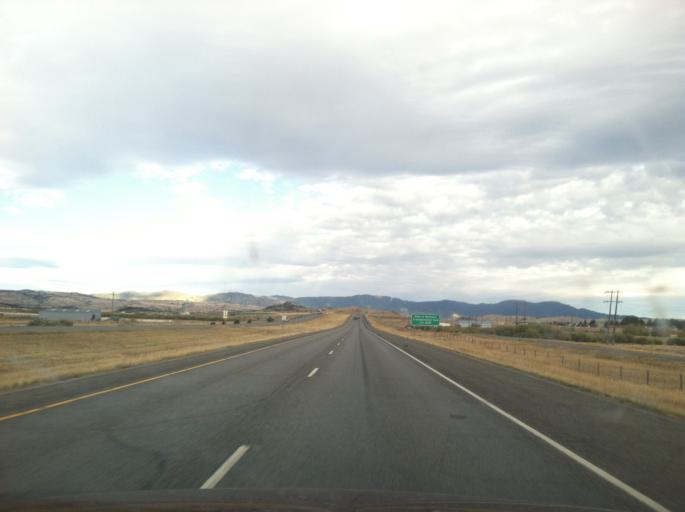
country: US
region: Montana
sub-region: Silver Bow County
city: Butte-Silver Bow (Balance)
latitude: 46.0100
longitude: -112.6994
